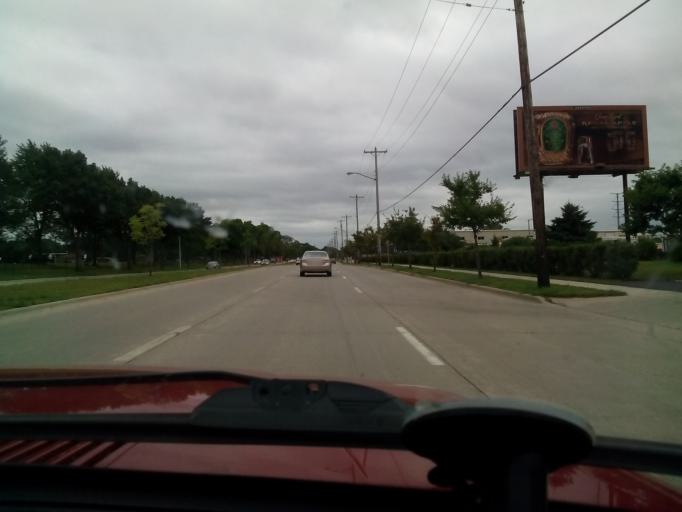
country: US
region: Wisconsin
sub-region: Dane County
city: Maple Bluff
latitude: 43.1017
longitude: -89.3592
